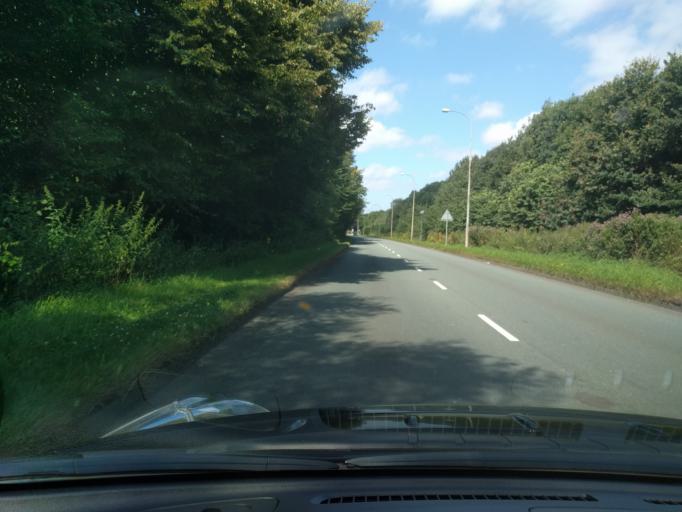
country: GB
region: England
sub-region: Warrington
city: Croft
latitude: 53.4077
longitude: -2.5261
